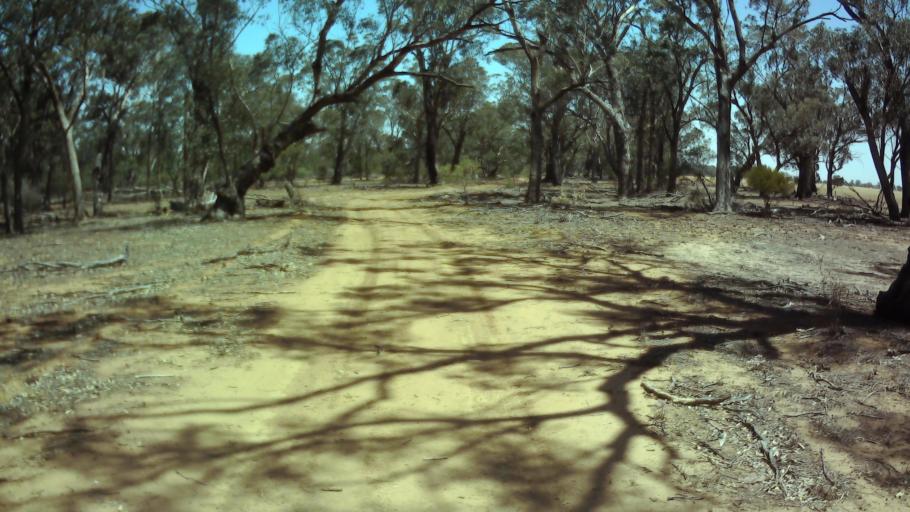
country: AU
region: New South Wales
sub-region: Weddin
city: Grenfell
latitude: -34.0650
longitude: 147.8022
